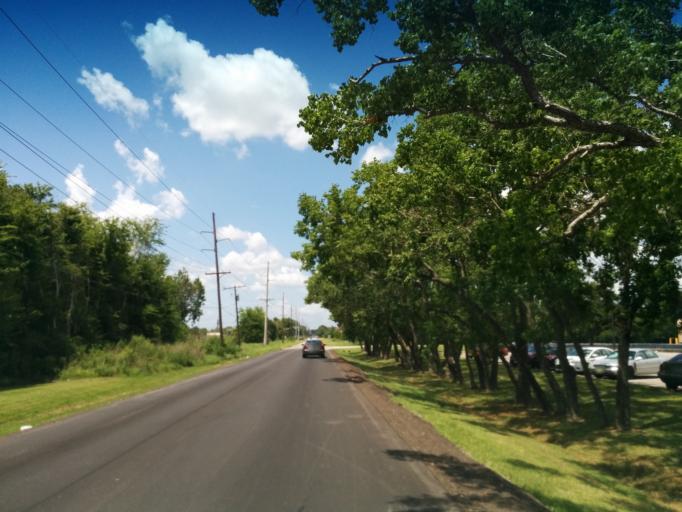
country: US
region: Texas
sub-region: Jefferson County
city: Beaumont
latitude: 30.1225
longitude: -94.1689
